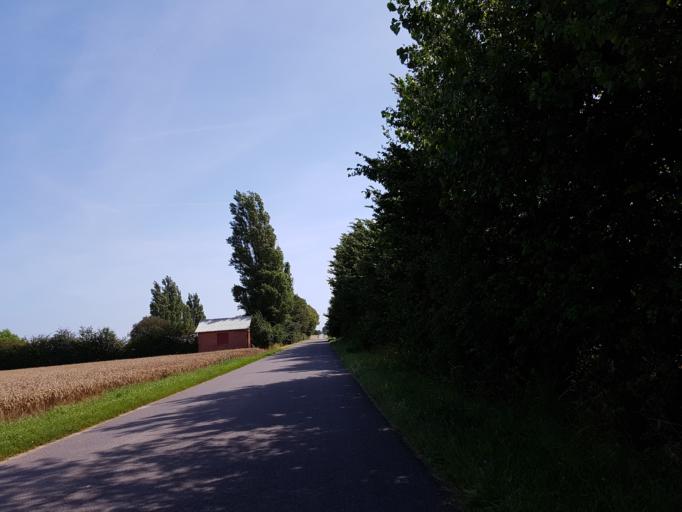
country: DK
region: Zealand
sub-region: Guldborgsund Kommune
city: Nykobing Falster
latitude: 54.5839
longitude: 11.9445
